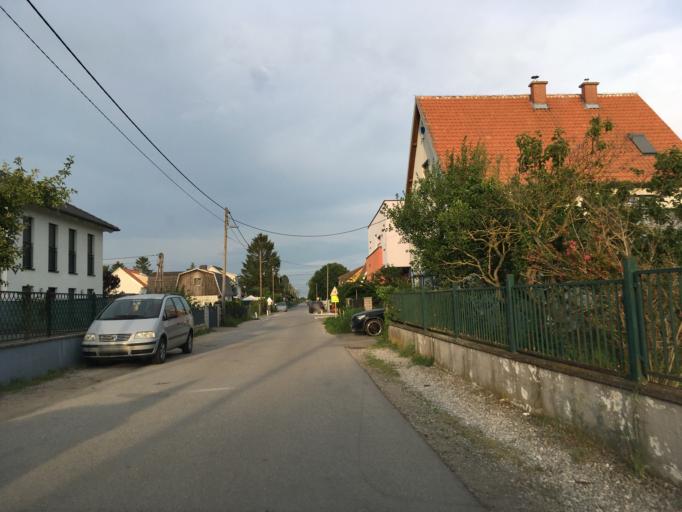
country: AT
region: Lower Austria
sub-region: Politischer Bezirk Wien-Umgebung
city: Gerasdorf bei Wien
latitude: 48.3136
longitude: 16.4957
